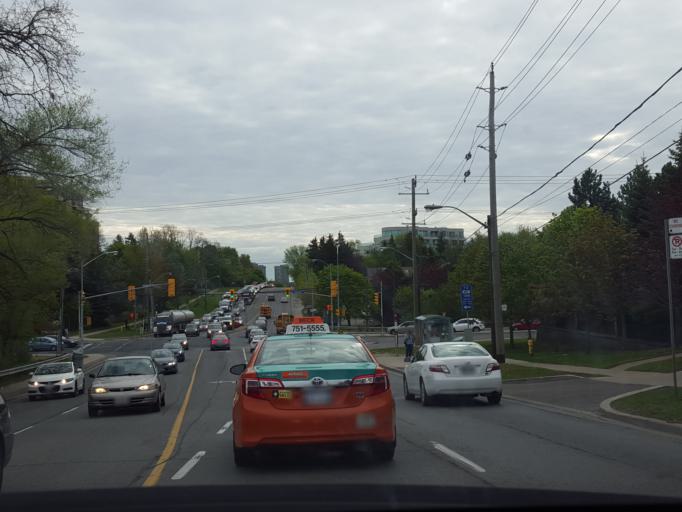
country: CA
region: Ontario
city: Willowdale
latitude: 43.7846
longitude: -79.3934
